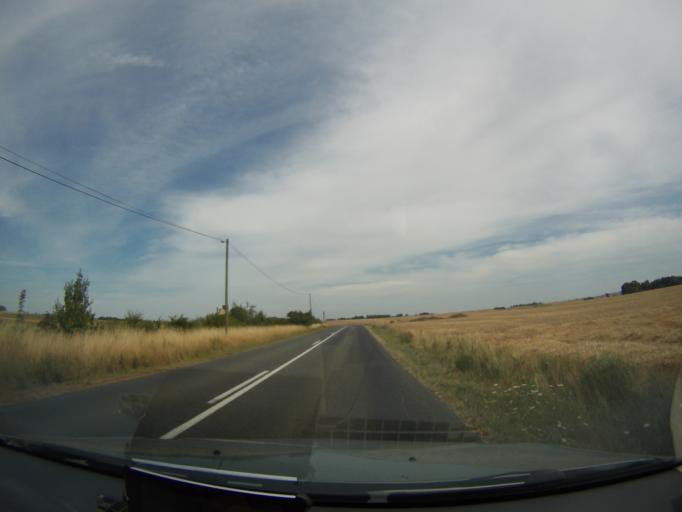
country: FR
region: Poitou-Charentes
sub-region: Departement de la Vienne
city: Saint-Jean-de-Sauves
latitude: 46.8016
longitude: 0.0839
